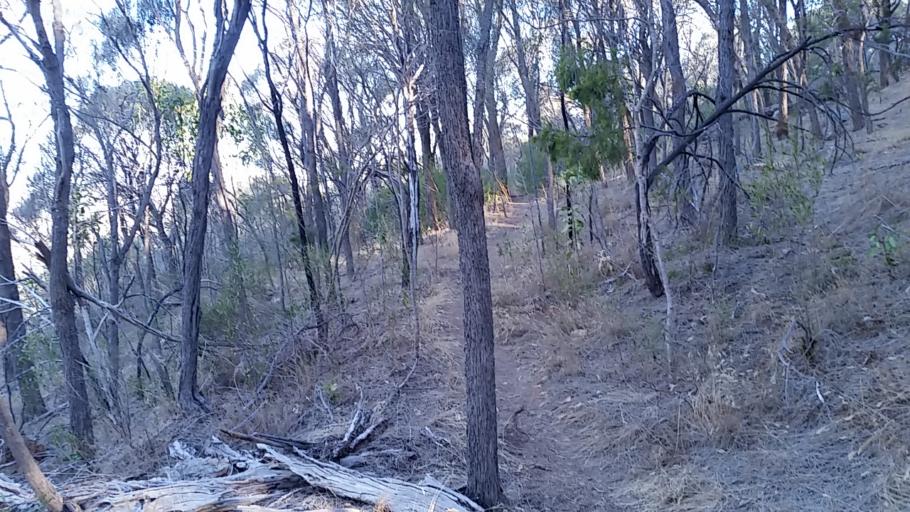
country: AU
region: South Australia
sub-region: Mount Barker
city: Nairne
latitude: -35.0641
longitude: 138.9223
